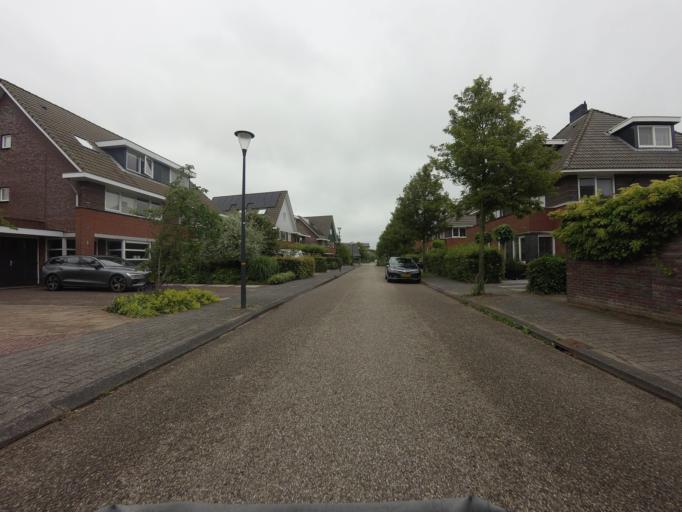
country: NL
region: North Holland
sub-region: Gemeente Schagen
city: Schagen
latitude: 52.7917
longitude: 4.8082
